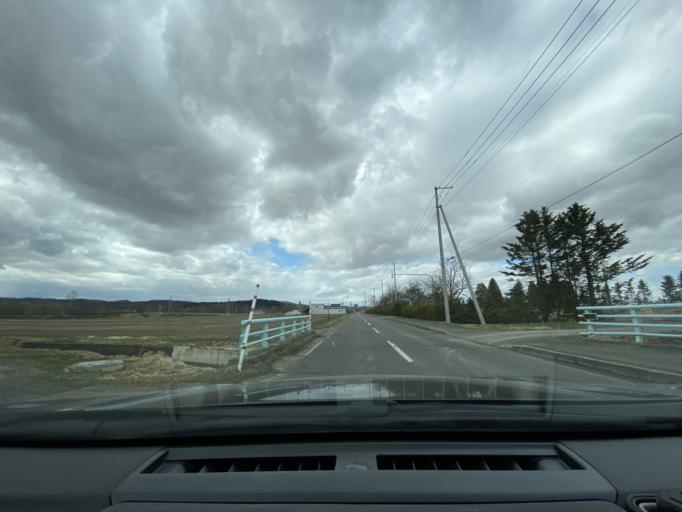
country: JP
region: Hokkaido
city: Nayoro
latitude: 44.1304
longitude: 142.4891
